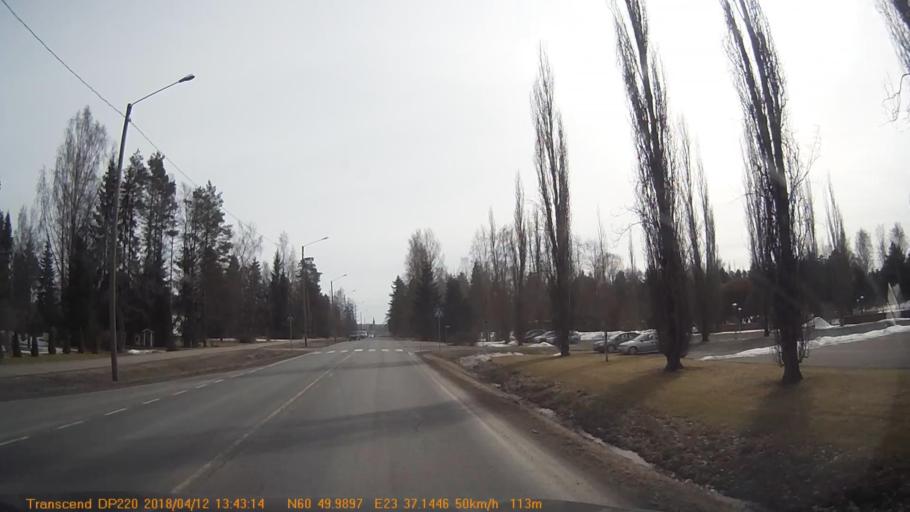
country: FI
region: Haeme
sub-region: Forssa
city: Forssa
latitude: 60.8327
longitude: 23.6193
